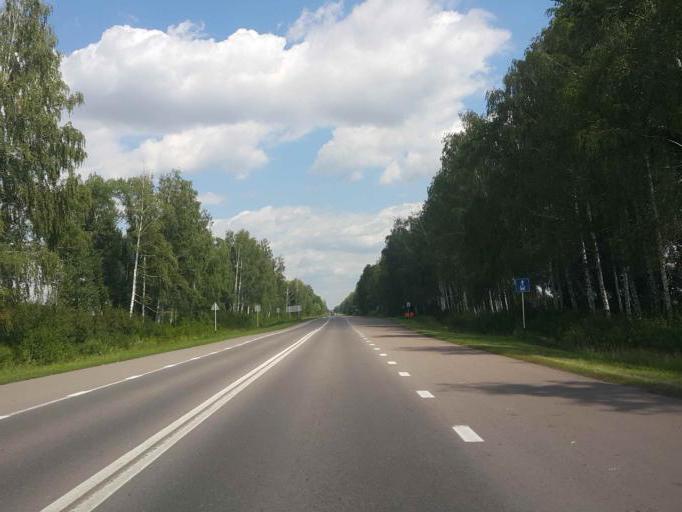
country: RU
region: Tambov
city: Goreloye
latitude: 53.0574
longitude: 41.4849
